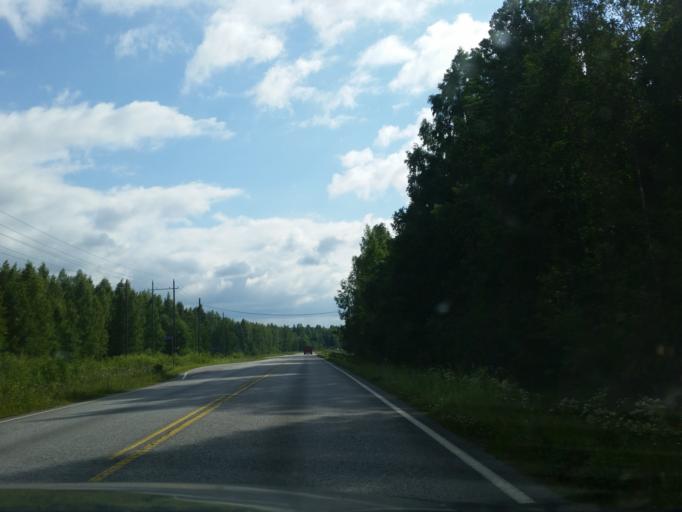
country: FI
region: Northern Savo
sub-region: Kuopio
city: Karttula
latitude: 62.9027
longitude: 26.9520
